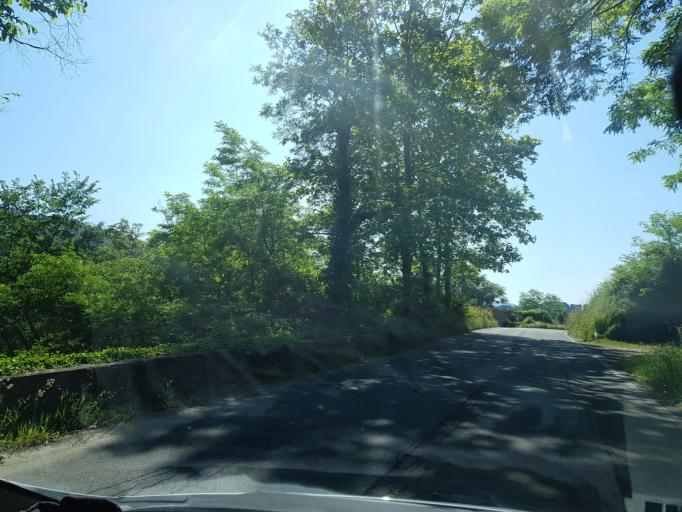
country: IT
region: Tuscany
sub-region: Provincia di Lucca
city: Camporgiano
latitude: 44.1636
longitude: 10.3286
